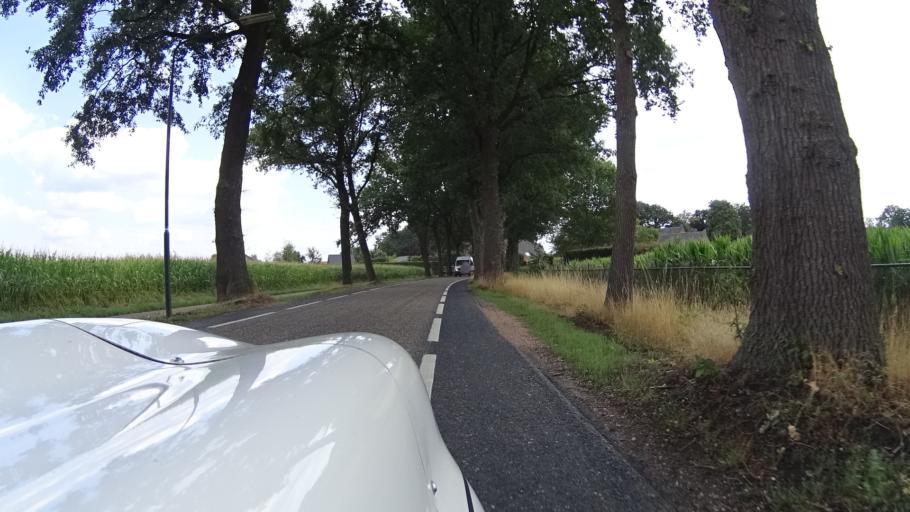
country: NL
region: North Brabant
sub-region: Gemeente Maasdonk
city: Geffen
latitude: 51.6949
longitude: 5.4544
